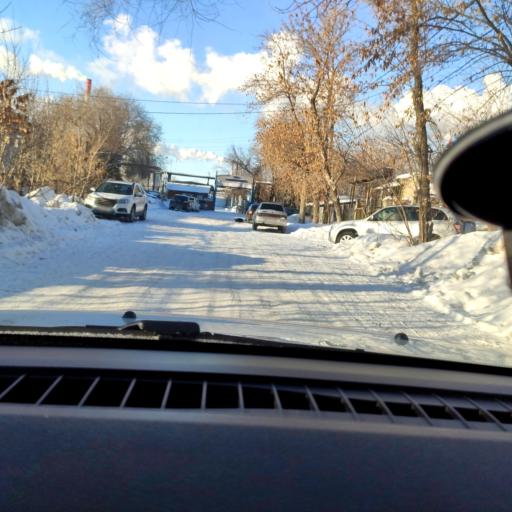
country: RU
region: Samara
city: Novokuybyshevsk
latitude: 53.1069
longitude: 50.0686
